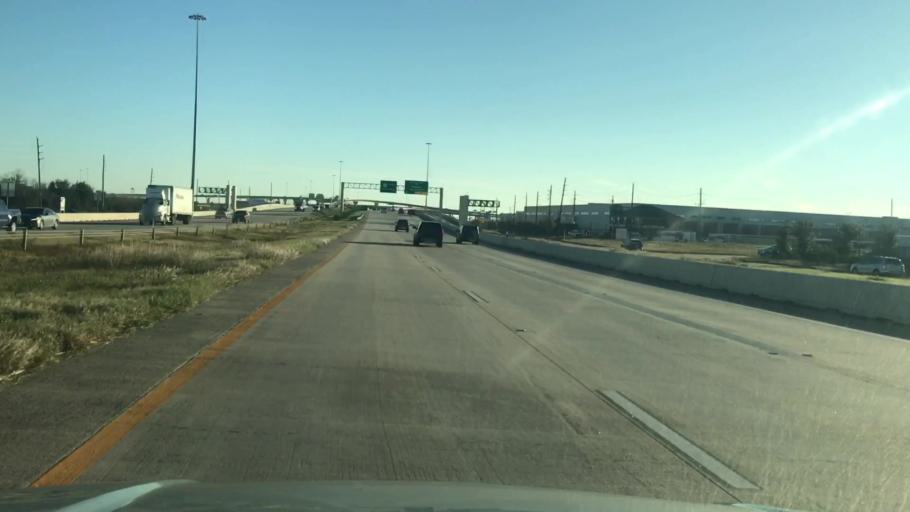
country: US
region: Texas
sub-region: Harris County
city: Katy
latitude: 29.7980
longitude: -95.7761
